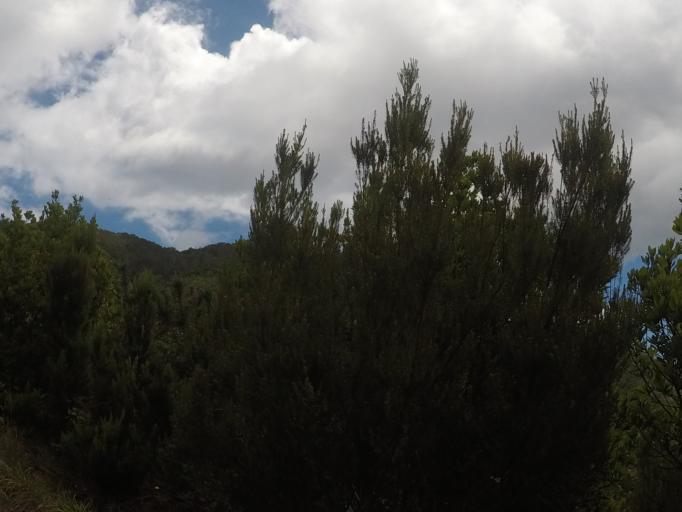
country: PT
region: Madeira
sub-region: Machico
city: Canical
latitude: 32.7547
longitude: -16.7712
